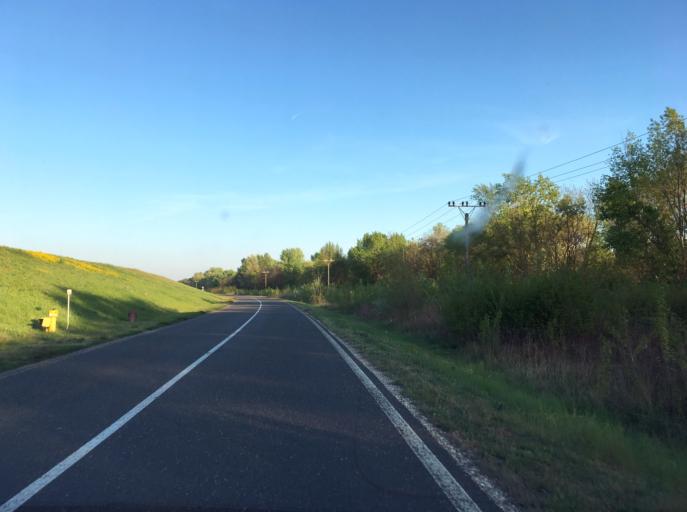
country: HU
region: Gyor-Moson-Sopron
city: Rajka
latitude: 48.0036
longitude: 17.2553
